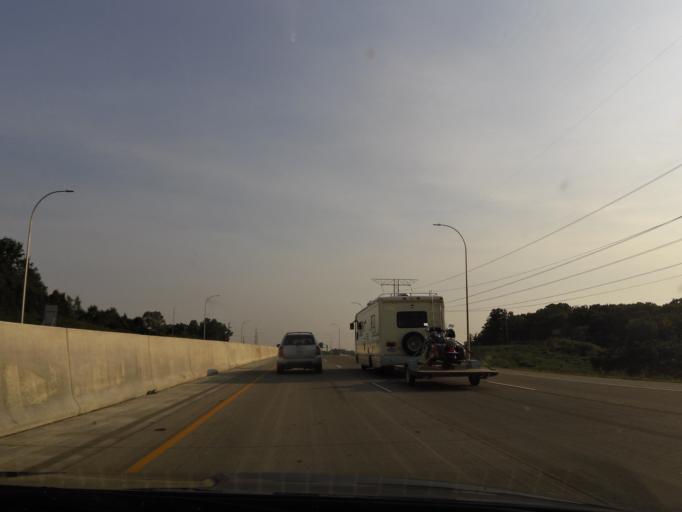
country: US
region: Minnesota
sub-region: Hennepin County
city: Plymouth
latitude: 45.0355
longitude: -93.4528
